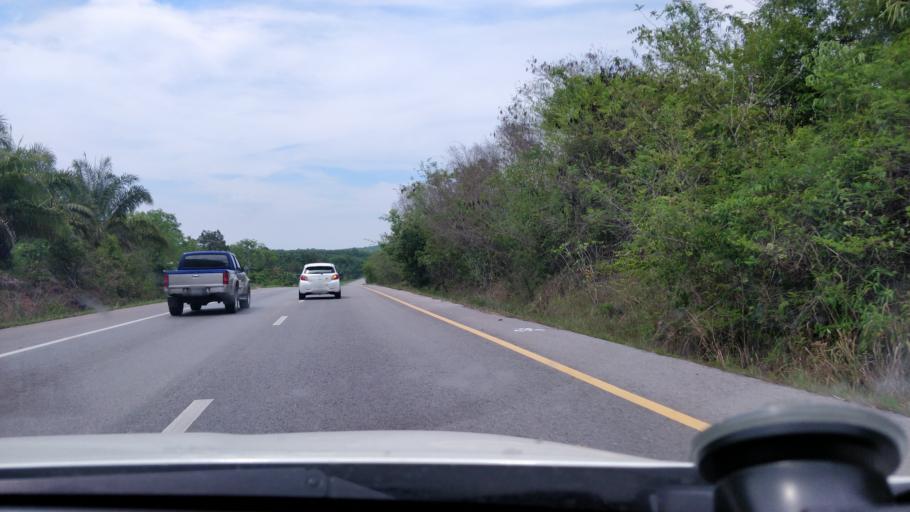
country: TH
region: Surat Thani
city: Khian Sa
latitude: 8.7982
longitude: 99.1620
